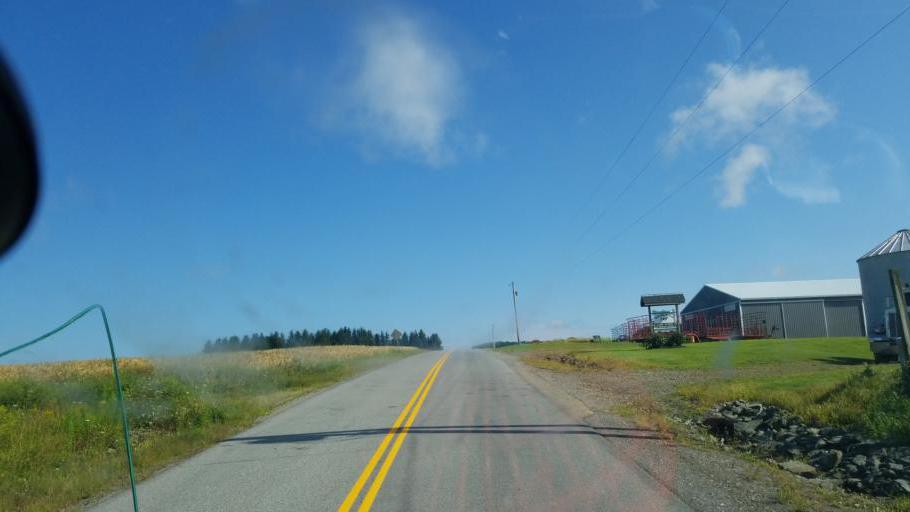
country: US
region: New York
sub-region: Allegany County
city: Andover
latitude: 42.1544
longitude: -77.7137
